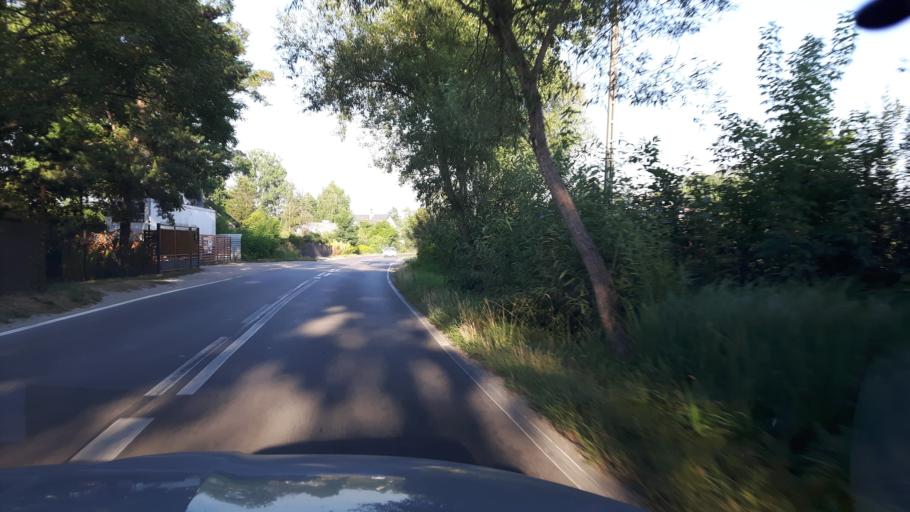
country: PL
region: Masovian Voivodeship
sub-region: Powiat wolominski
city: Kobylka
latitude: 52.3594
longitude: 21.1806
